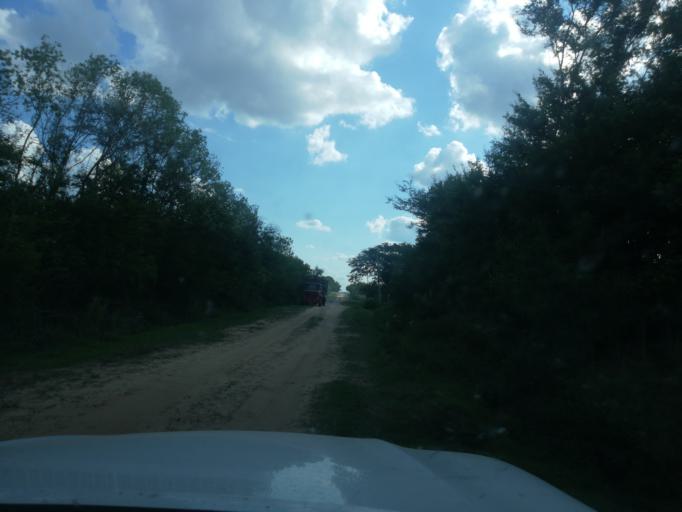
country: AR
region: Corrientes
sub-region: Departamento de San Miguel
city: San Miguel
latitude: -27.9899
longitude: -57.5689
